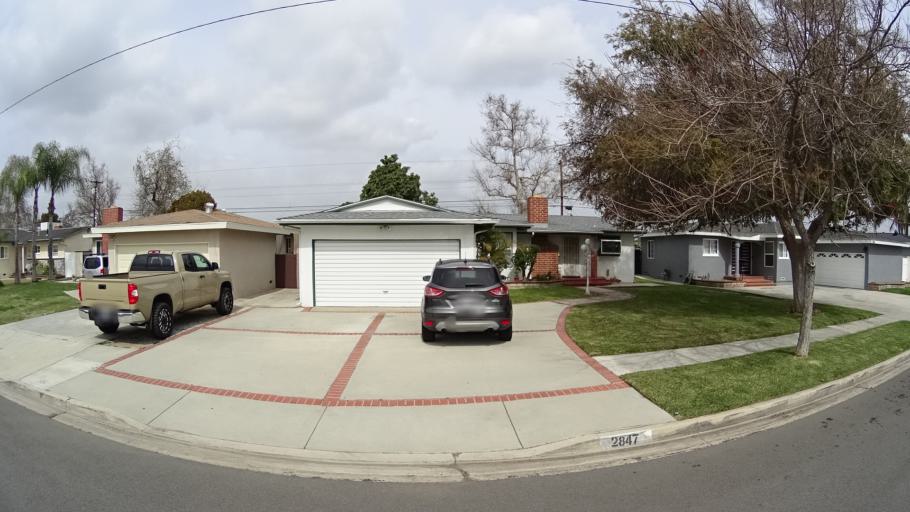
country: US
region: California
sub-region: Orange County
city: Stanton
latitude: 33.8281
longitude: -117.9873
